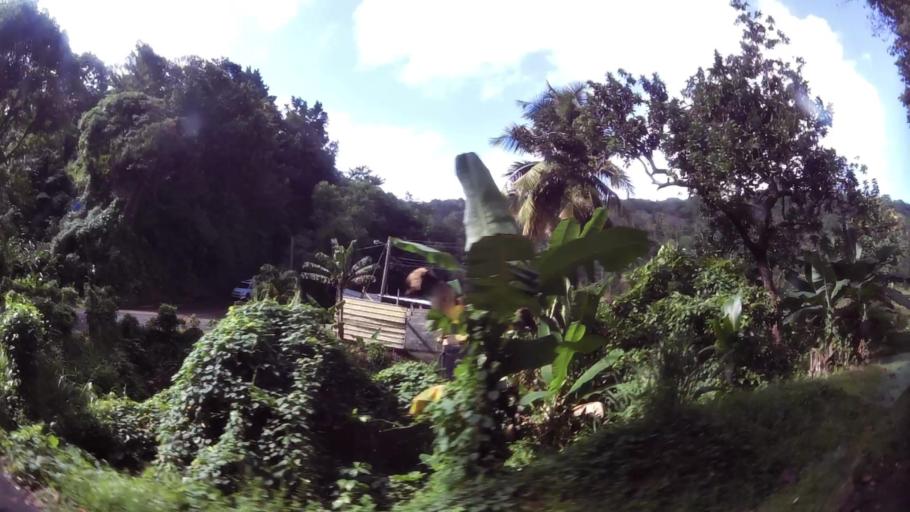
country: DM
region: Saint Andrew
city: Marigot
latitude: 15.5144
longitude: -61.2694
